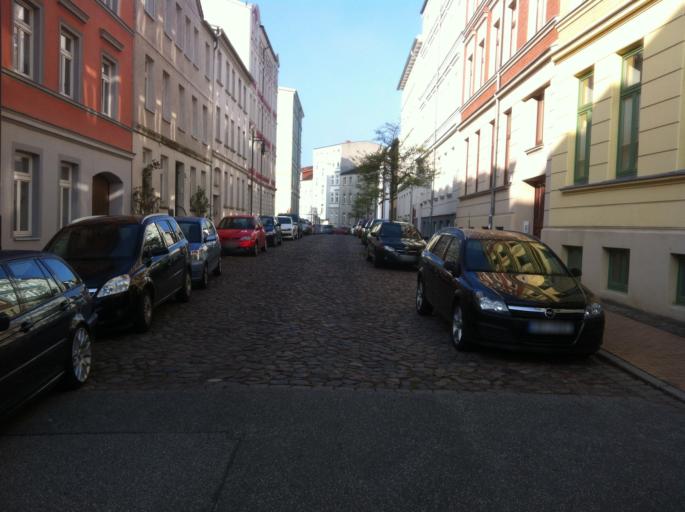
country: DE
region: Mecklenburg-Vorpommern
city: Feldstadt
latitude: 53.6227
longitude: 11.4048
